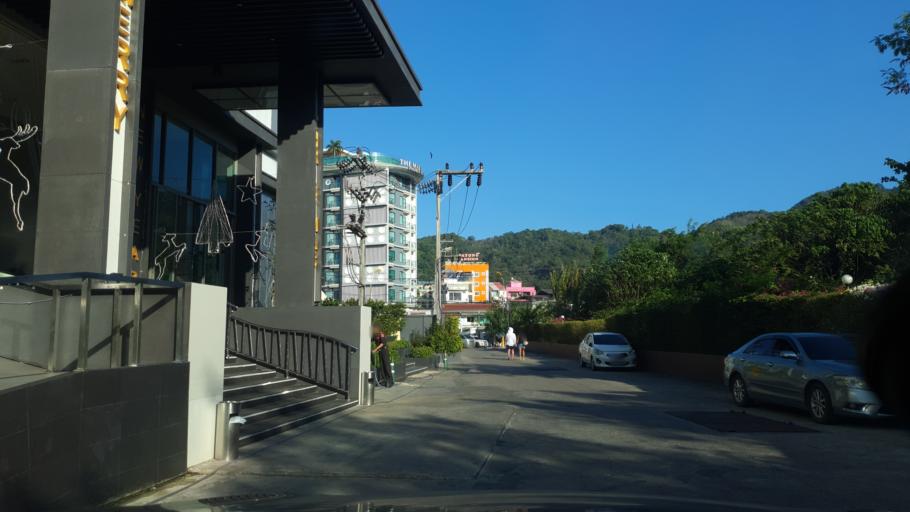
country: TH
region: Phuket
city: Patong
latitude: 7.8991
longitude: 98.3025
